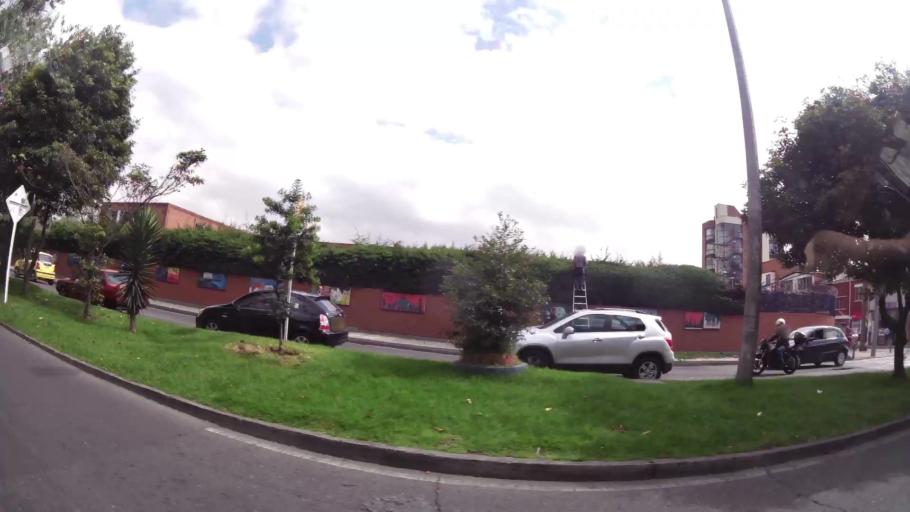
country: CO
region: Bogota D.C.
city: Bogota
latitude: 4.6337
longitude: -74.0742
